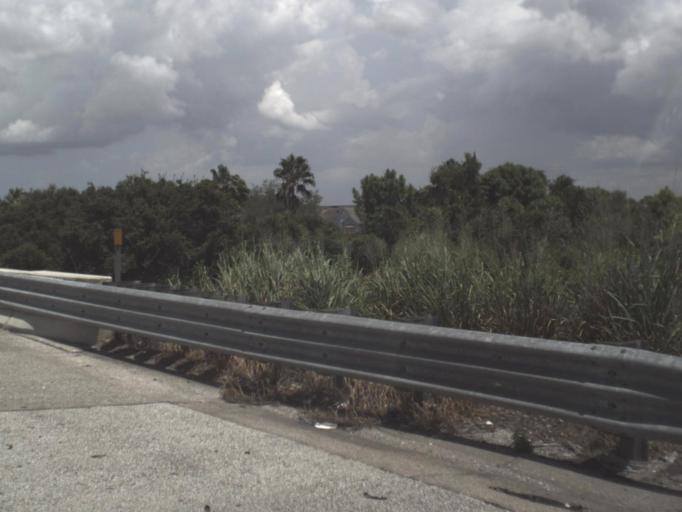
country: US
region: Florida
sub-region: Hillsborough County
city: Mango
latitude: 27.9498
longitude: -82.3280
